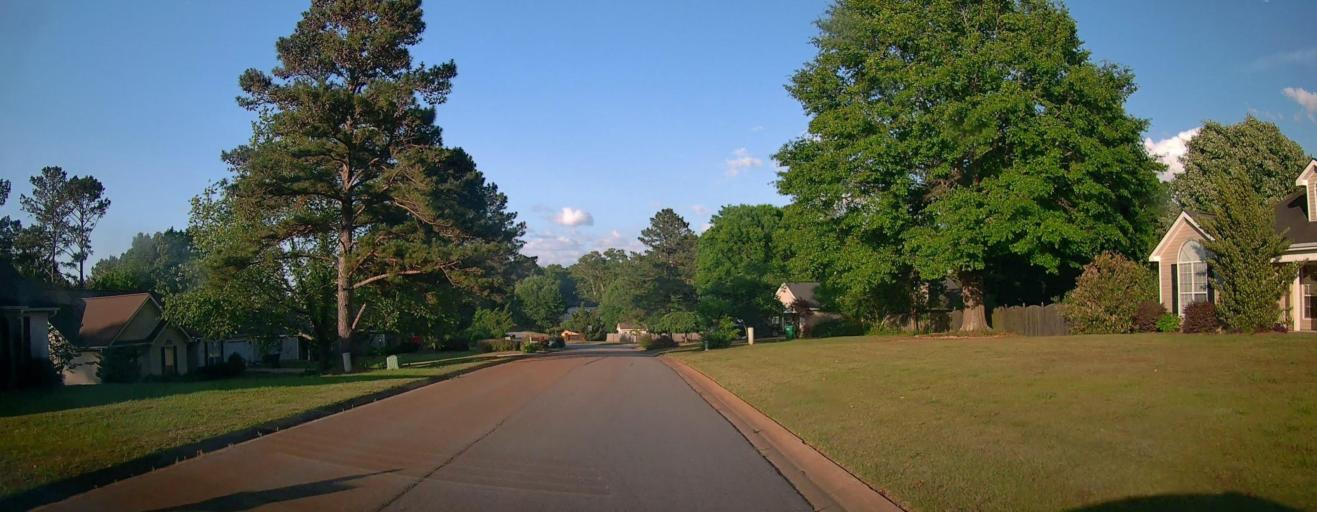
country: US
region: Georgia
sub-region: Houston County
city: Centerville
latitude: 32.6380
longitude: -83.7184
